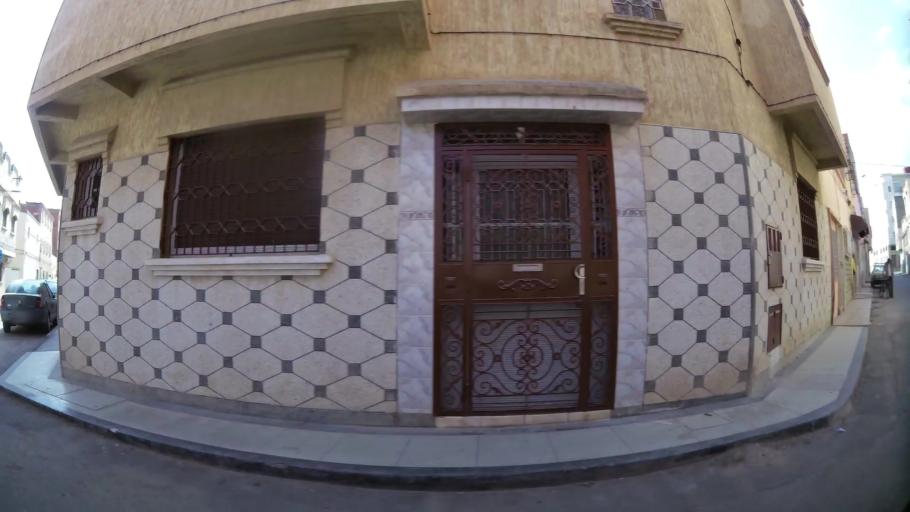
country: MA
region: Oriental
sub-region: Oujda-Angad
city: Oujda
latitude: 34.6865
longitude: -1.9075
